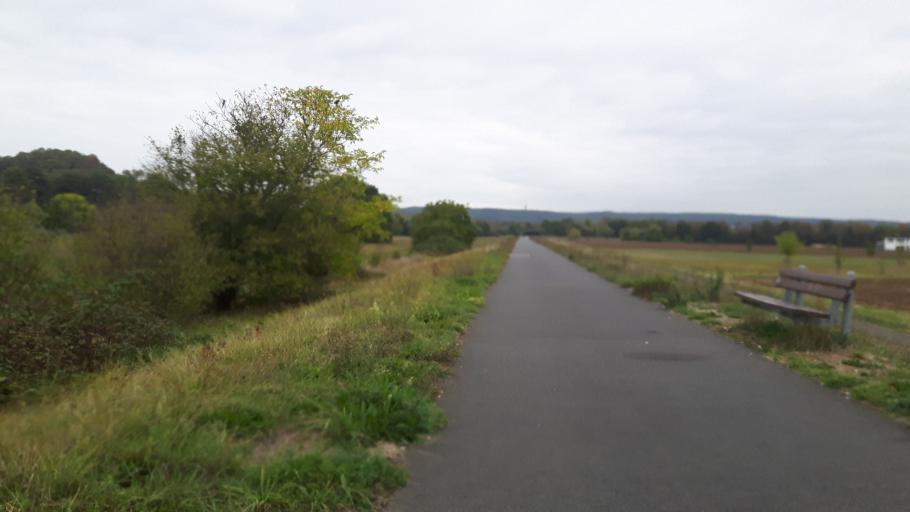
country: DE
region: North Rhine-Westphalia
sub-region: Regierungsbezirk Koln
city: Siegburg
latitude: 50.7866
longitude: 7.2273
